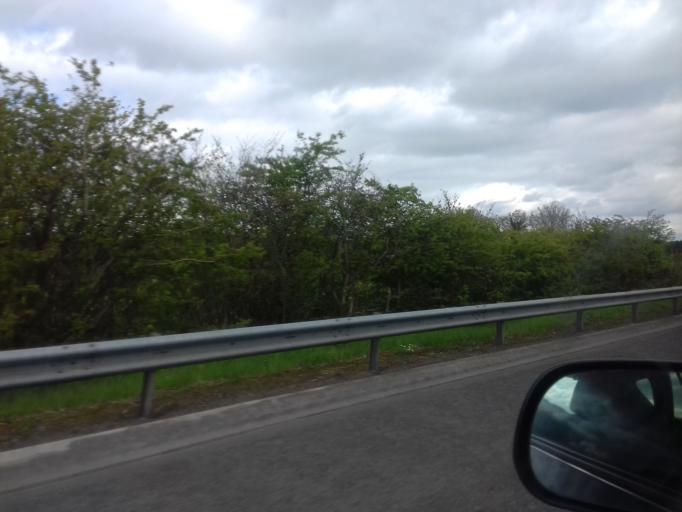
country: IE
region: Leinster
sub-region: Kildare
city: Cherryville
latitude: 53.1523
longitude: -6.9710
